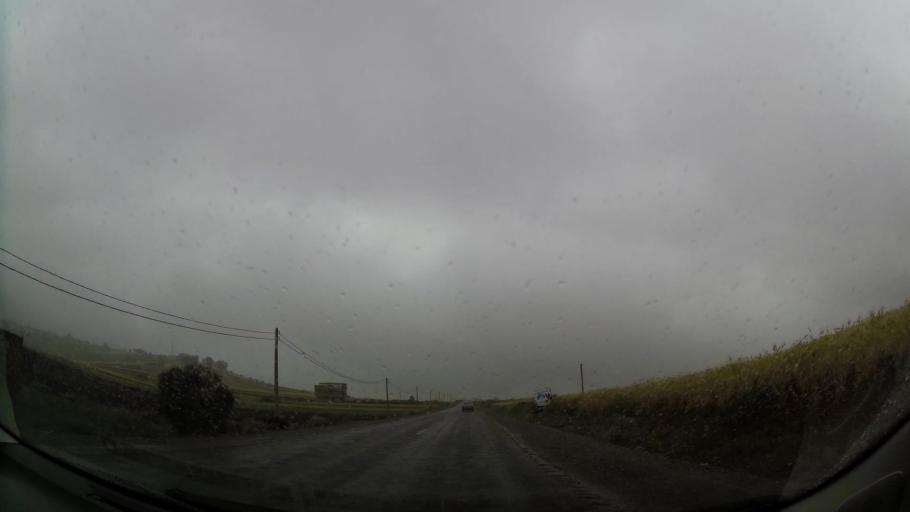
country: MA
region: Oriental
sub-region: Nador
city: Boudinar
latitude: 35.1373
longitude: -3.6211
